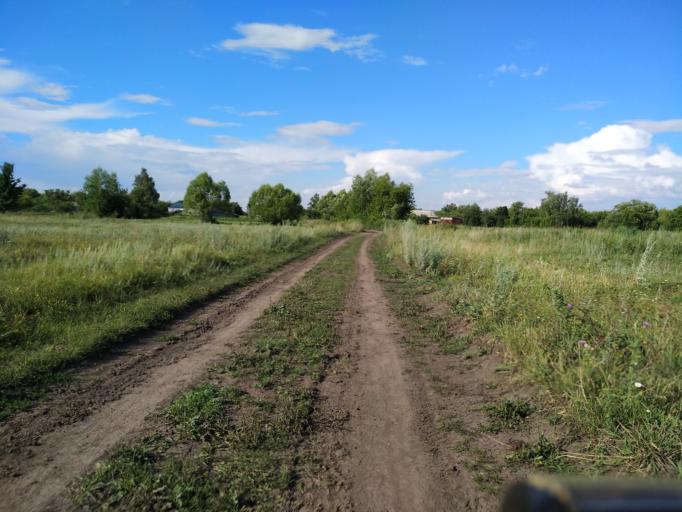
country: RU
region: Lipetsk
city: Dobrinka
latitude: 52.0272
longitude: 40.5613
